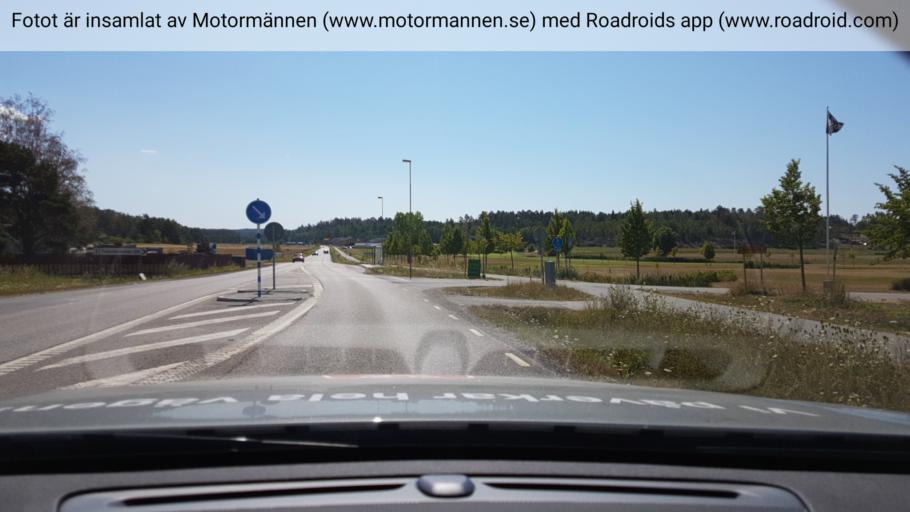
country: SE
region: Stockholm
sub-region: Ekero Kommun
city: Ekeroe
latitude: 59.3156
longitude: 17.7708
